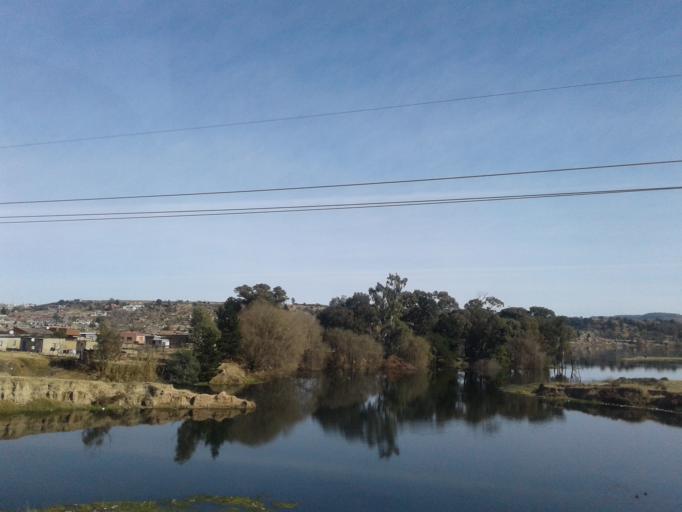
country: LS
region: Maseru
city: Maseru
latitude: -29.3026
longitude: 27.5164
